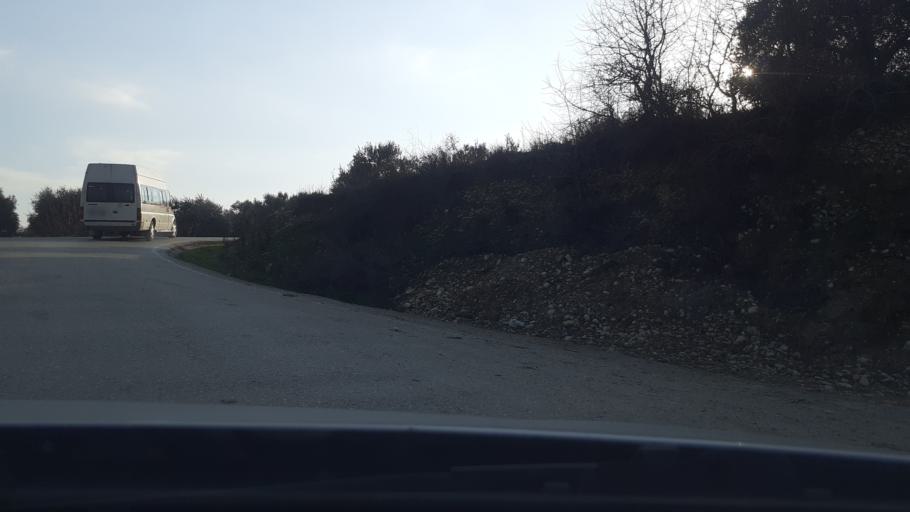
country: TR
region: Hatay
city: Boynuyogun
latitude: 36.1417
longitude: 36.3181
